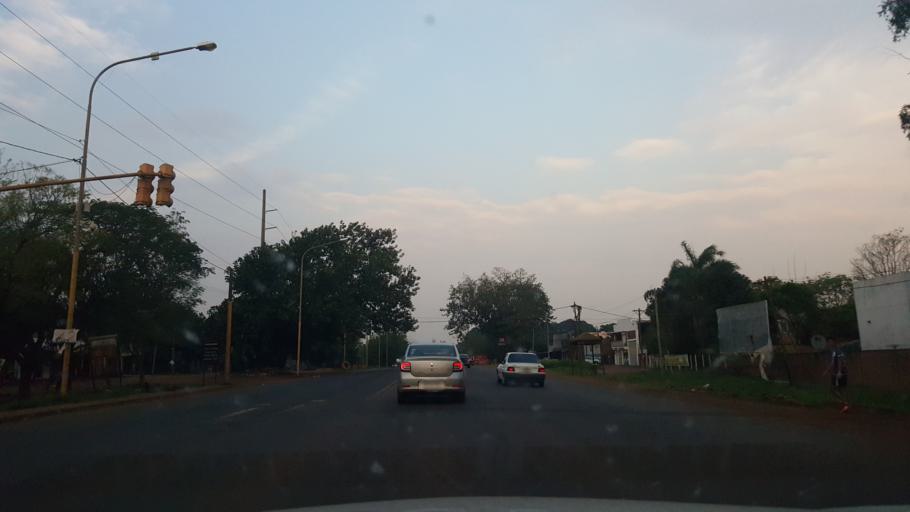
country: AR
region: Misiones
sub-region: Departamento de Capital
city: Posadas
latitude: -27.4007
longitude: -55.9365
